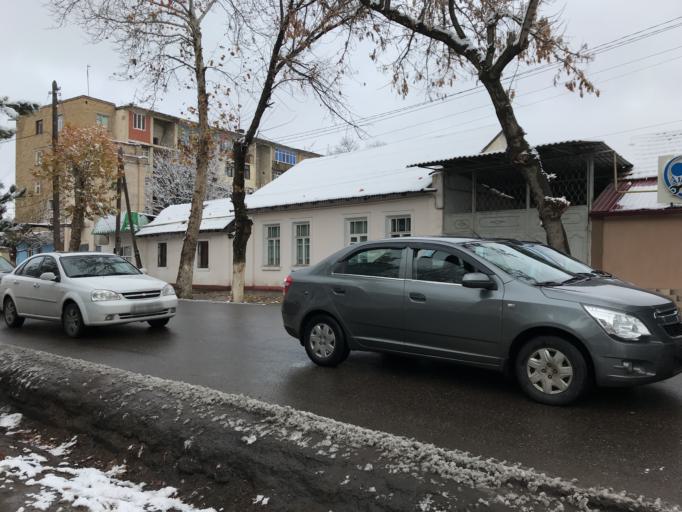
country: UZ
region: Toshkent
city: Yangiyul
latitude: 41.1097
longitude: 69.0523
